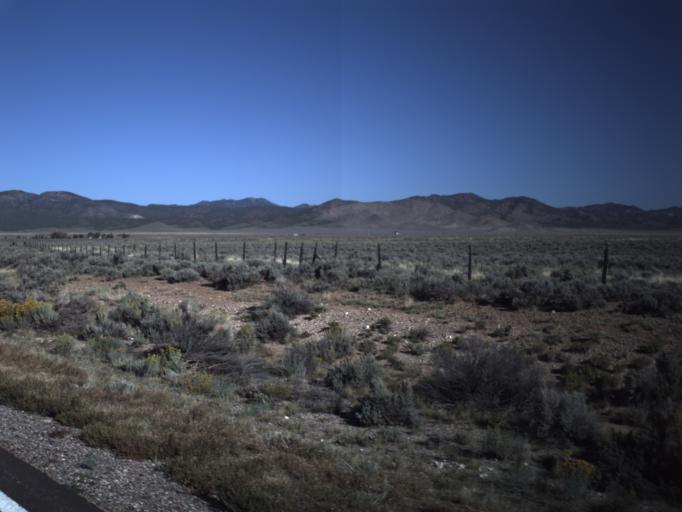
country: US
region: Utah
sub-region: Washington County
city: Enterprise
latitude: 37.7881
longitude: -113.8805
